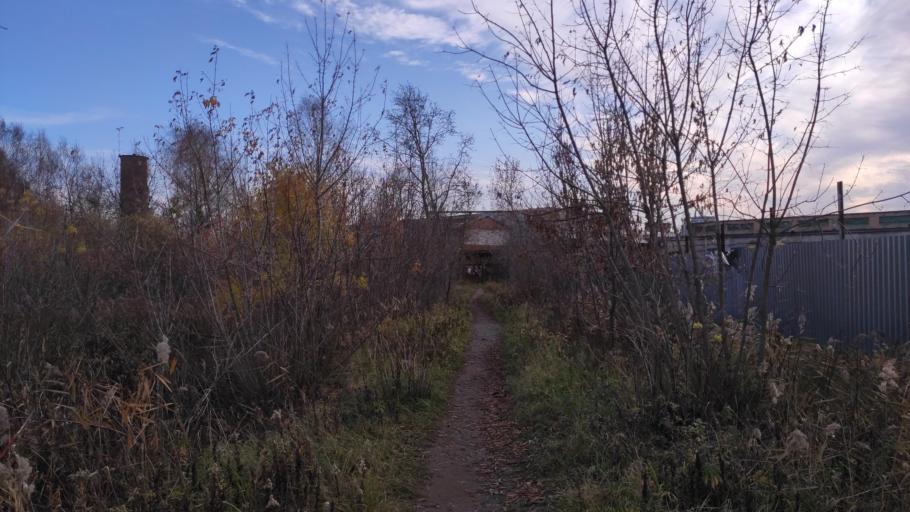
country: RU
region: Moskovskaya
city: Noginsk
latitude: 55.8747
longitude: 38.4569
